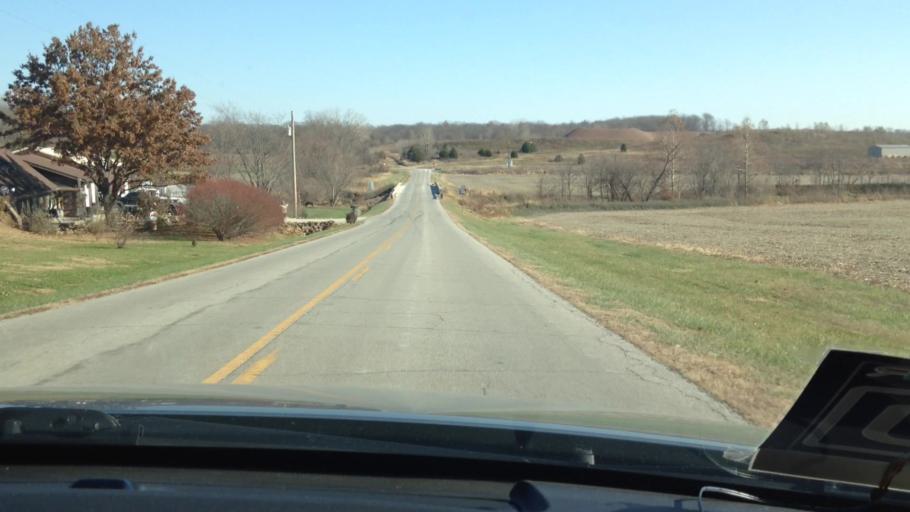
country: US
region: Missouri
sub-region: Platte County
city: Weston
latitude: 39.4980
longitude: -94.8065
